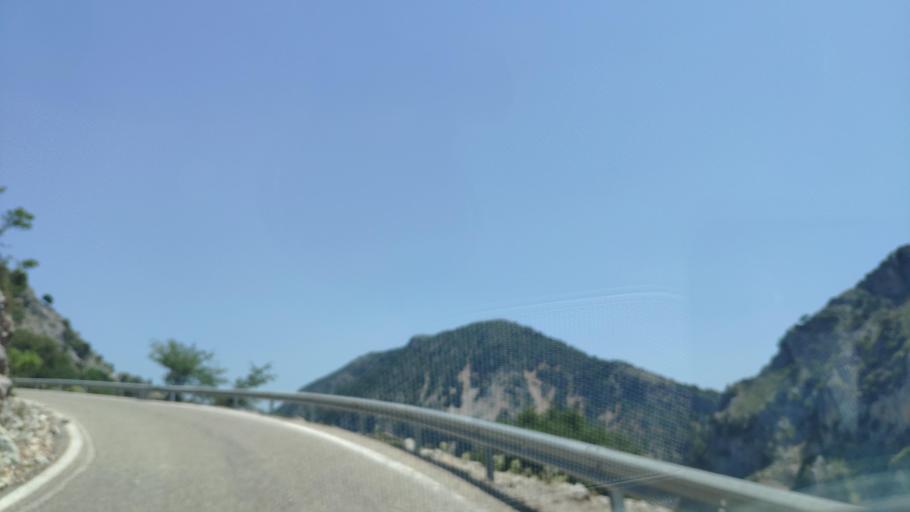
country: GR
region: West Greece
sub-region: Nomos Aitolias kai Akarnanias
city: Krikellos
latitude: 39.0078
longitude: 21.3717
